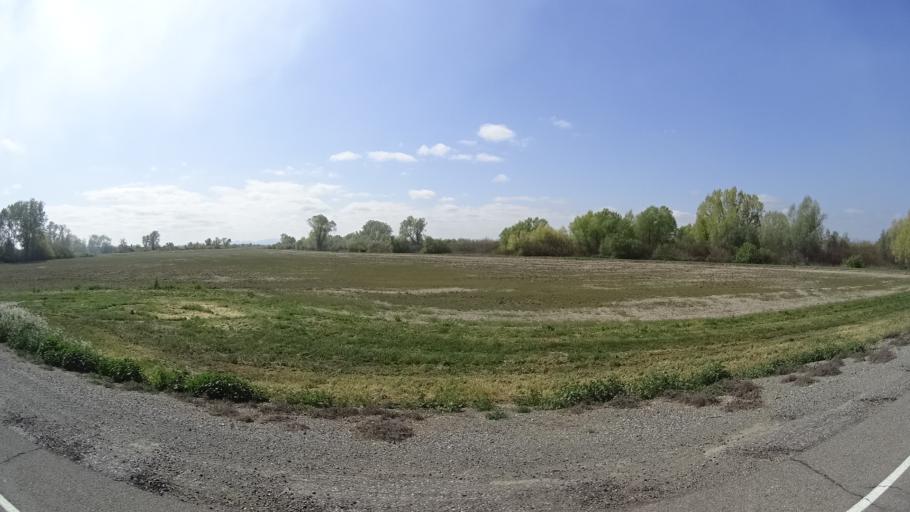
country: US
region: California
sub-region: Butte County
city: Biggs
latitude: 39.4642
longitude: -121.9224
